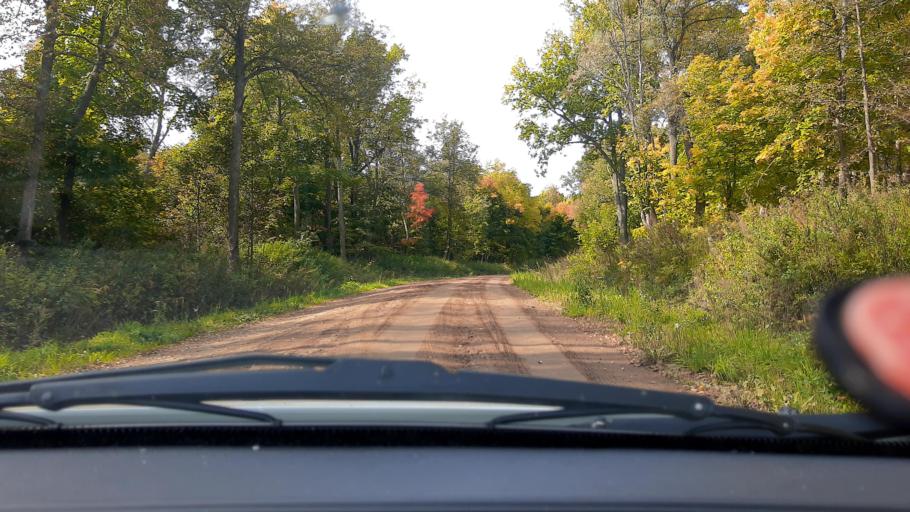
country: RU
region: Bashkortostan
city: Kudeyevskiy
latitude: 54.7137
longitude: 56.6248
